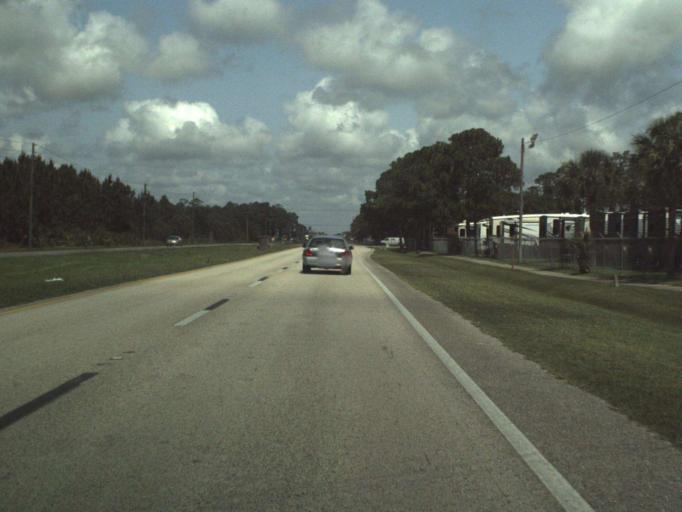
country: US
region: Florida
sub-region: Volusia County
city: Ormond-by-the-Sea
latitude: 29.3271
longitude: -81.1190
